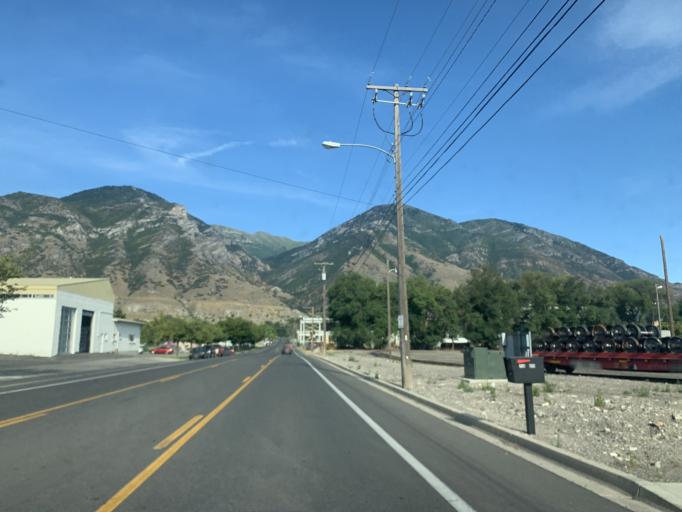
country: US
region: Utah
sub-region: Utah County
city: Provo
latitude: 40.2256
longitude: -111.6529
